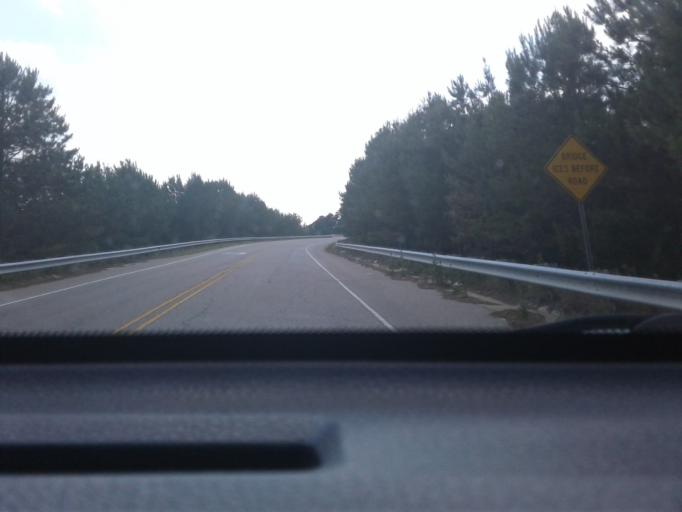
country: US
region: North Carolina
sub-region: Cumberland County
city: Eastover
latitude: 35.1202
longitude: -78.7554
